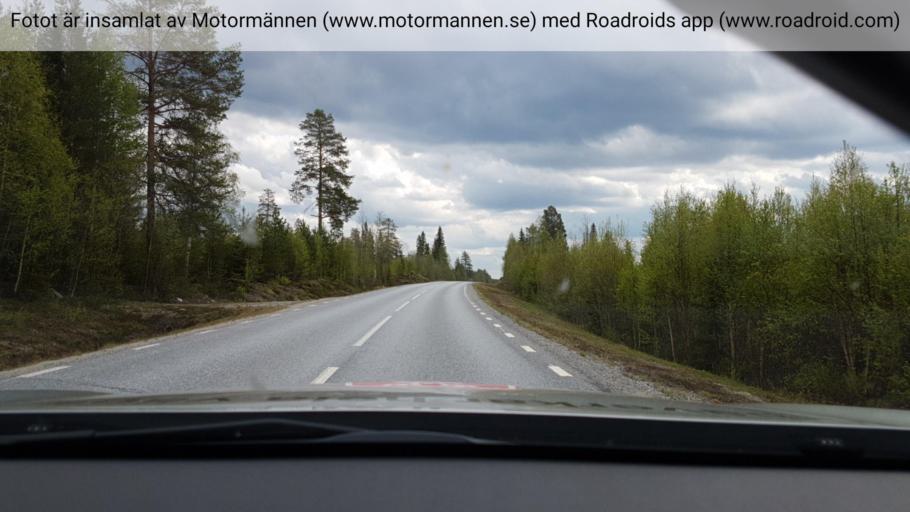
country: SE
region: Vaesterbotten
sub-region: Bjurholms Kommun
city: Bjurholm
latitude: 64.0084
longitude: 18.7197
